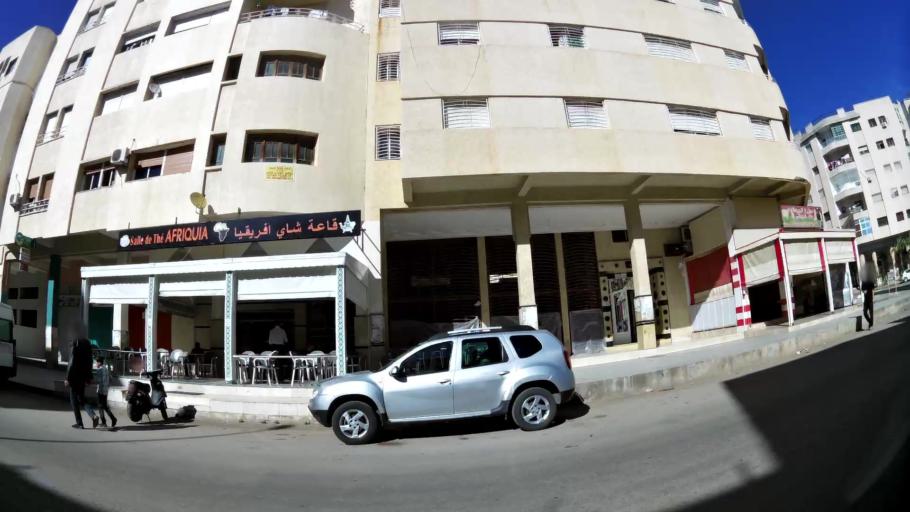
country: MA
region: Fes-Boulemane
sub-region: Fes
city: Fes
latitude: 34.0110
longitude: -4.9664
